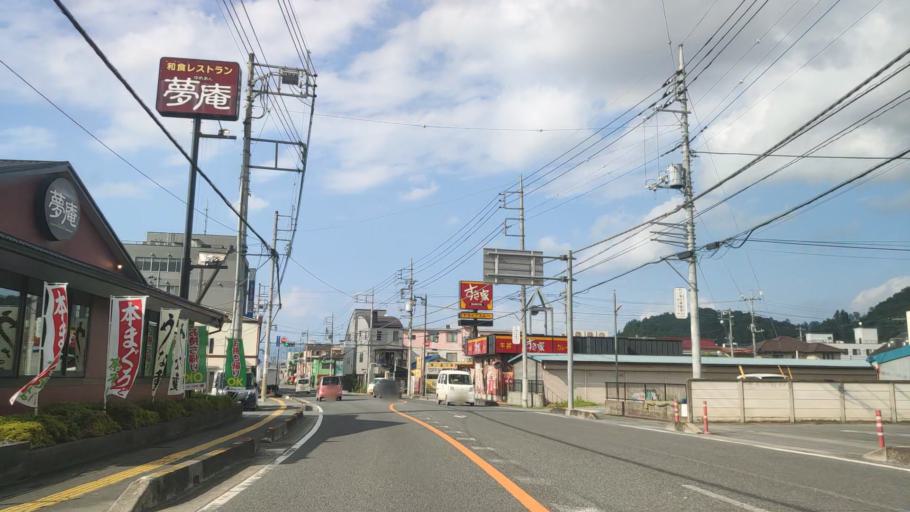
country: JP
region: Saitama
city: Chichibu
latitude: 35.9893
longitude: 139.0854
